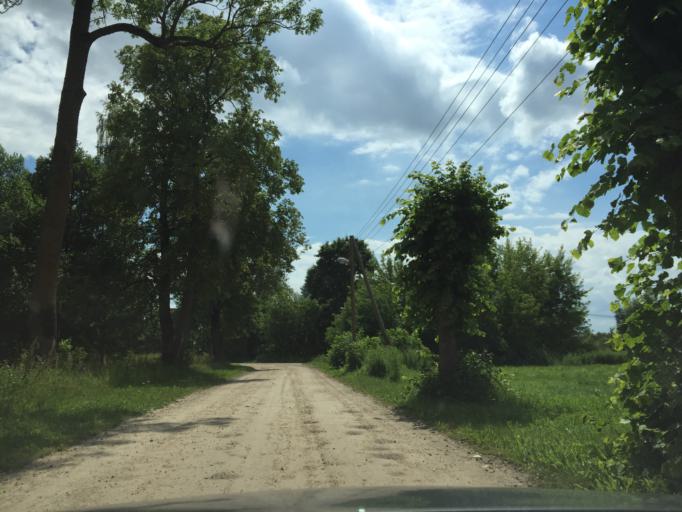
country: LV
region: Jelgava
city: Jelgava
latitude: 56.6473
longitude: 23.6801
